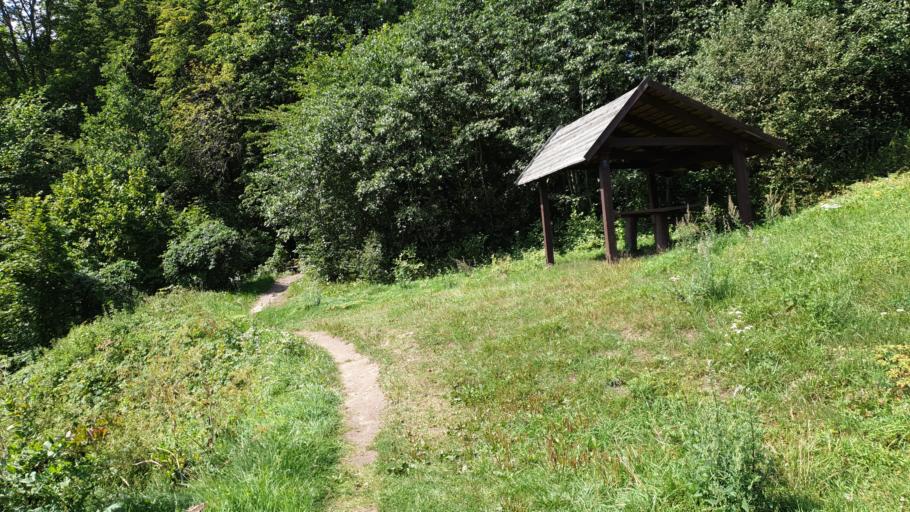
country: LT
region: Vilnius County
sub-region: Vilniaus Rajonas
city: Vievis
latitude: 54.8266
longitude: 24.9438
